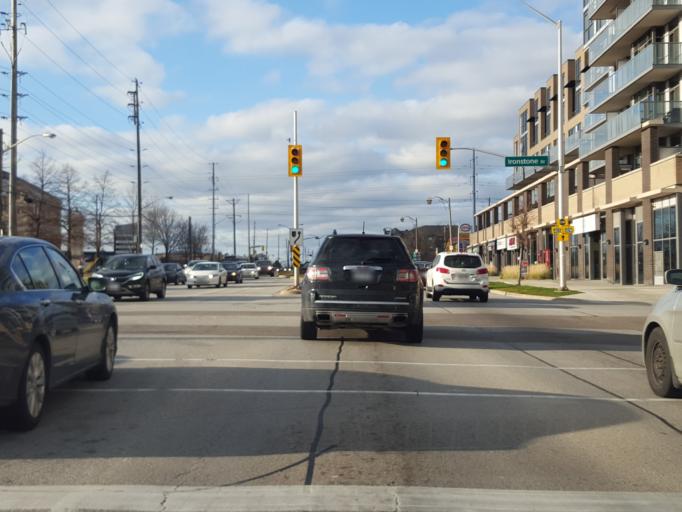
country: CA
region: Ontario
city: Burlington
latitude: 43.3924
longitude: -79.7882
